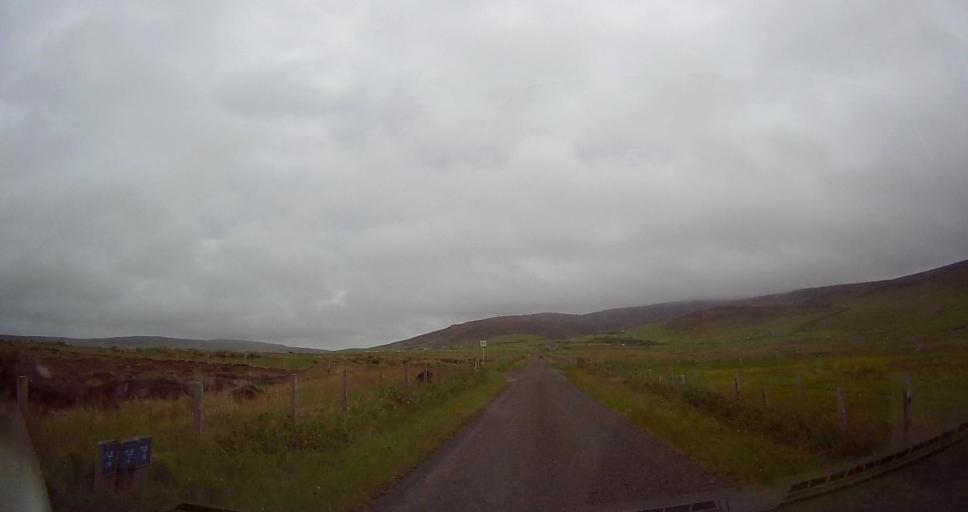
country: GB
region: Scotland
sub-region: Orkney Islands
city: Stromness
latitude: 58.9839
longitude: -3.1863
